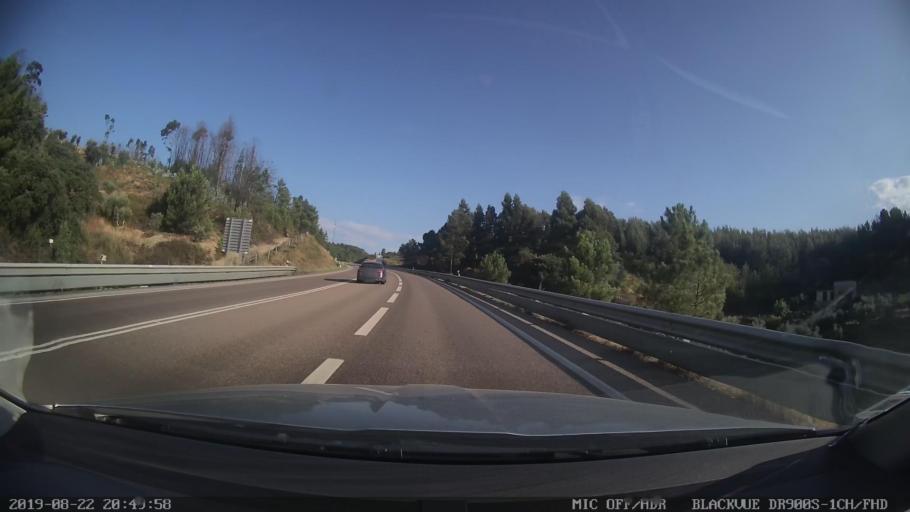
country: PT
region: Castelo Branco
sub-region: Proenca-A-Nova
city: Proenca-a-Nova
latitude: 39.7493
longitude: -7.9345
